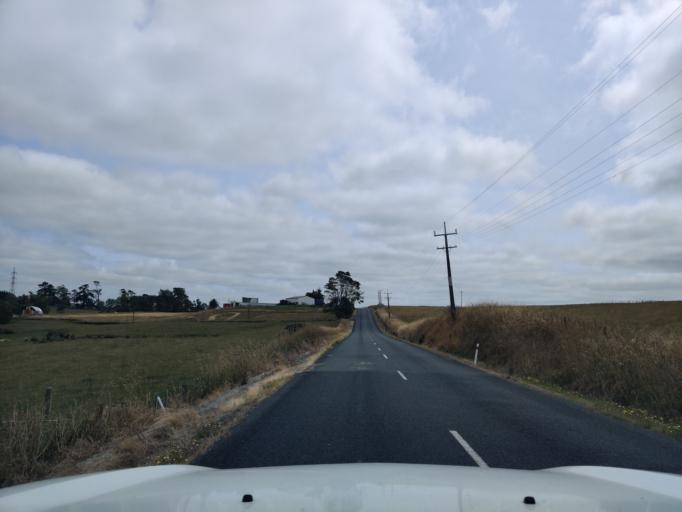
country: NZ
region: Waikato
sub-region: Waikato District
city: Te Kauwhata
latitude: -37.5101
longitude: 175.1799
